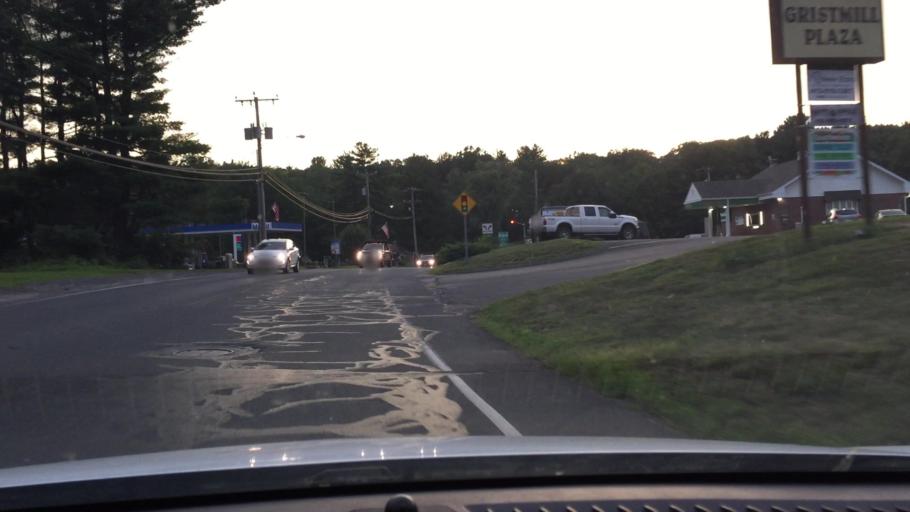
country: US
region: Massachusetts
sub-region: Hampden County
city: Southwick
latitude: 42.0598
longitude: -72.7625
